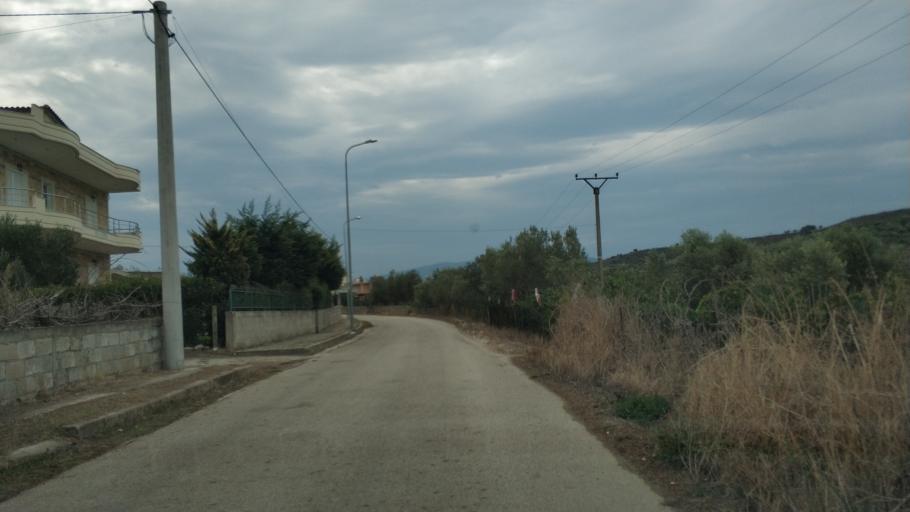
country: AL
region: Vlore
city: Vlore
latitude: 40.5108
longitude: 19.4102
